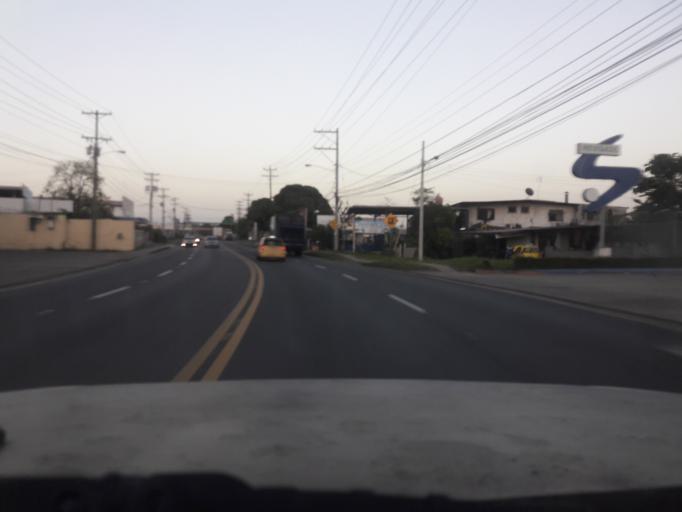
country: PA
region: Panama
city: San Miguelito
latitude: 9.0468
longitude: -79.4414
